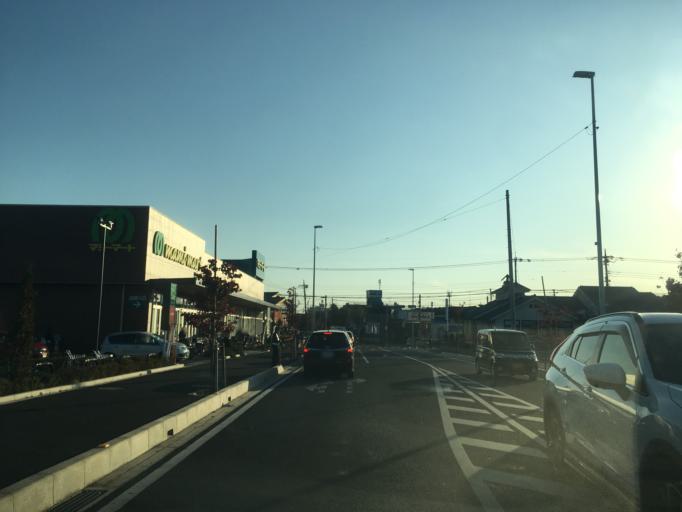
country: JP
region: Saitama
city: Tokorozawa
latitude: 35.8082
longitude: 139.4381
